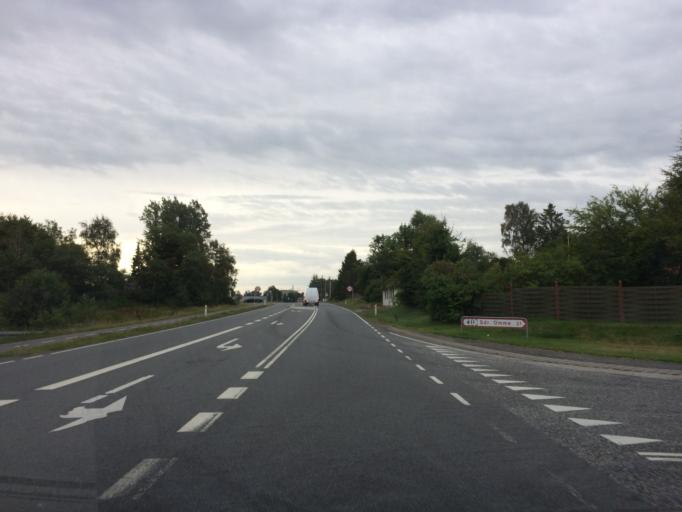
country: DK
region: Central Jutland
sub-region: Ikast-Brande Kommune
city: Brande
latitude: 55.9578
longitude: 9.1070
